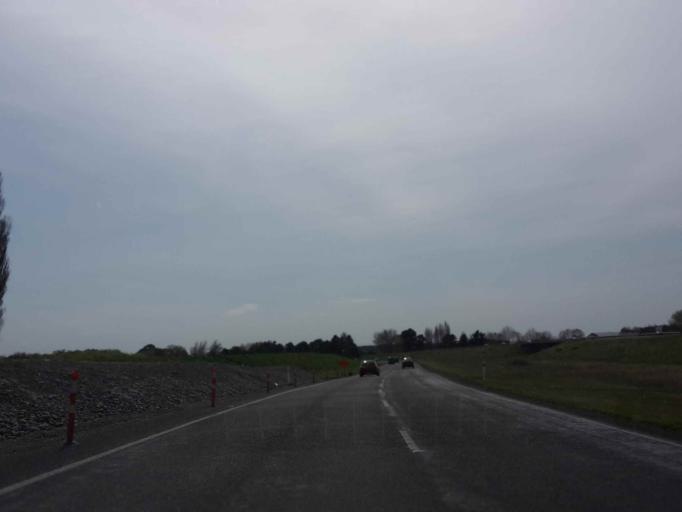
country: NZ
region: Canterbury
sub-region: Waimakariri District
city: Kaiapoi
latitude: -43.4318
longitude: 172.6418
